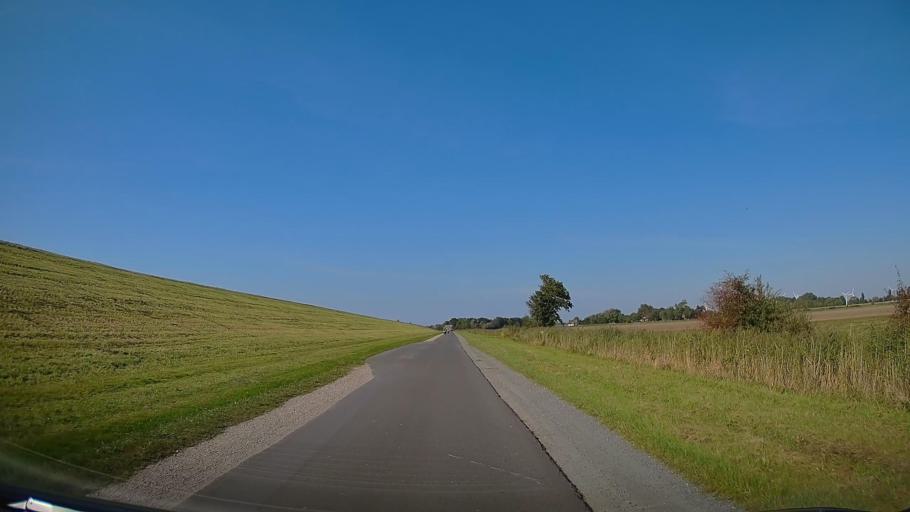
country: DE
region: Lower Saxony
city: Wremen
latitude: 53.6516
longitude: 8.4945
